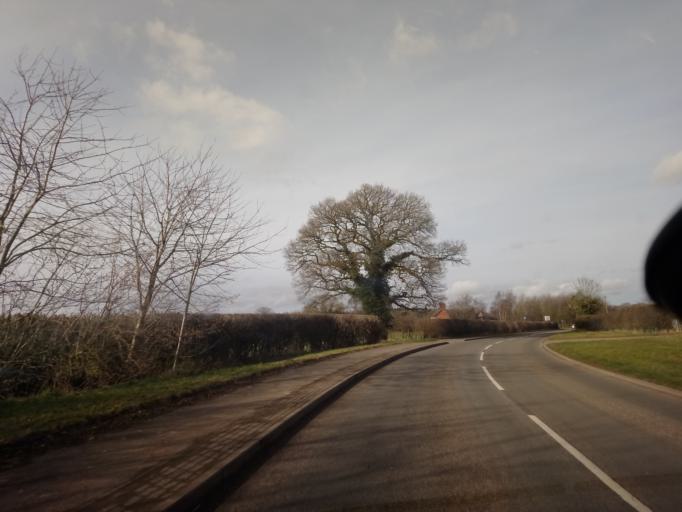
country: GB
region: England
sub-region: Shropshire
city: Stoke upon Tern
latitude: 52.8453
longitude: -2.5737
